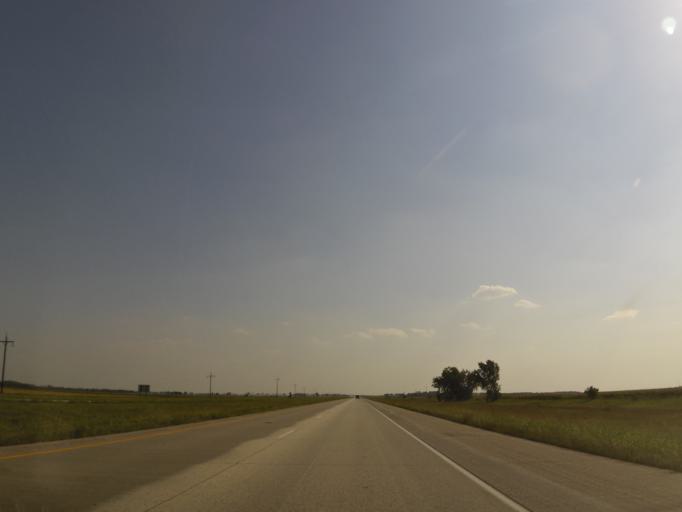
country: US
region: North Dakota
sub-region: Walsh County
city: Grafton
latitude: 48.3425
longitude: -97.1897
